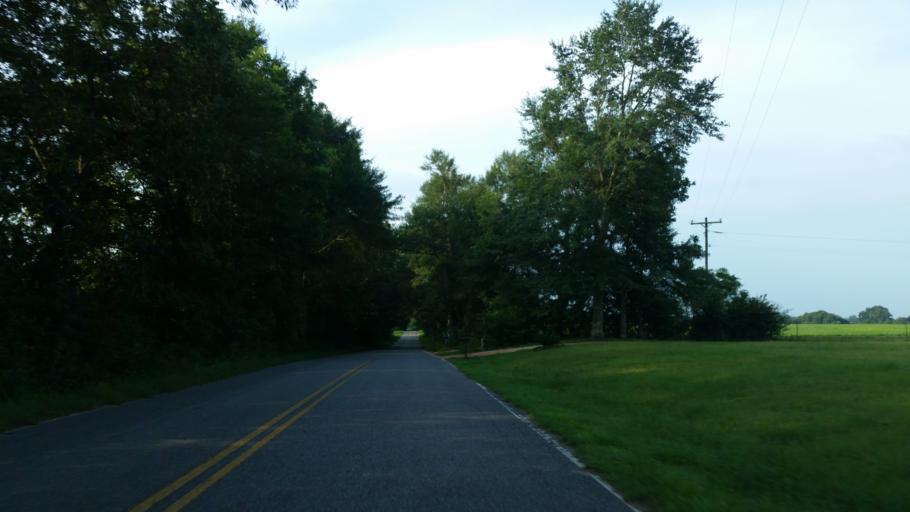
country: US
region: Alabama
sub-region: Escambia County
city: Atmore
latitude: 30.9965
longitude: -87.5711
